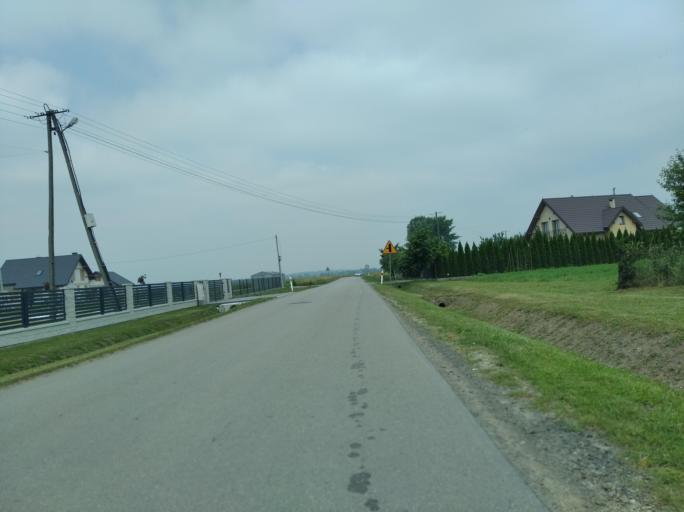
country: PL
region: Subcarpathian Voivodeship
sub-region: Powiat sanocki
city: Besko
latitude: 49.5996
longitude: 21.9581
